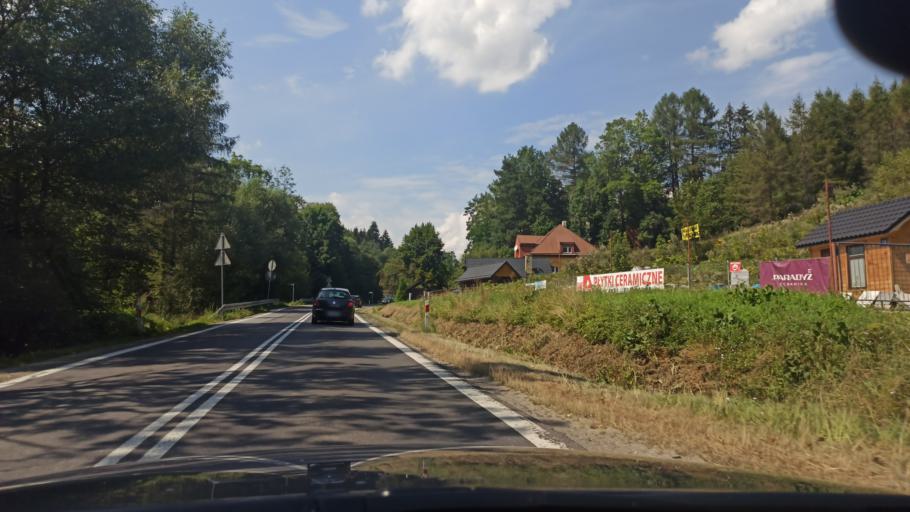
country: PL
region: Lesser Poland Voivodeship
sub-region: Powiat nowotarski
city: Krosnica
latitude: 49.4384
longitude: 20.3601
